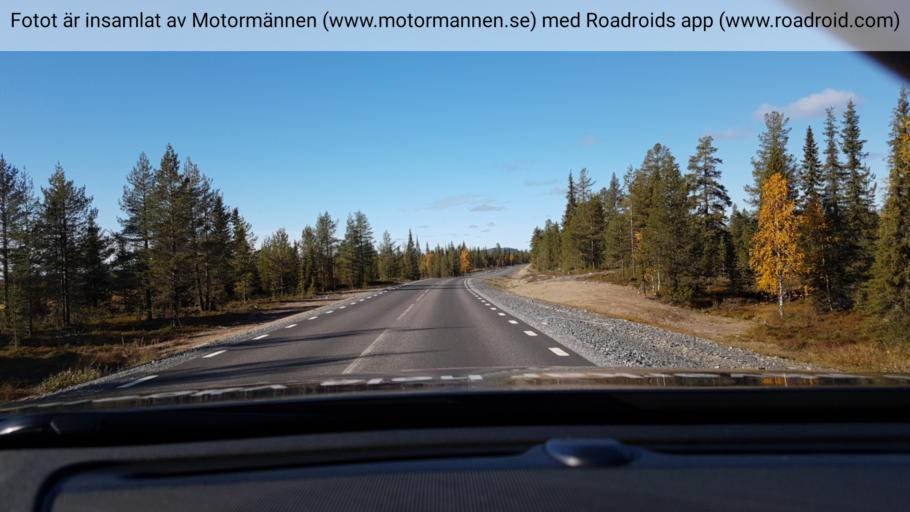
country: SE
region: Norrbotten
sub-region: Gallivare Kommun
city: Gaellivare
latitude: 66.9386
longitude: 20.8285
